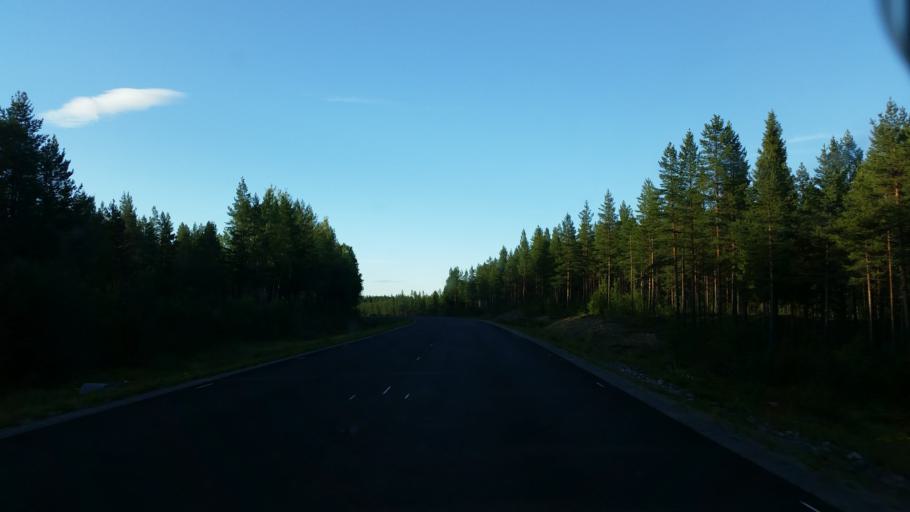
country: SE
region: Vaesterbotten
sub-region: Dorotea Kommun
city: Dorotea
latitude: 64.2713
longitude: 16.5007
